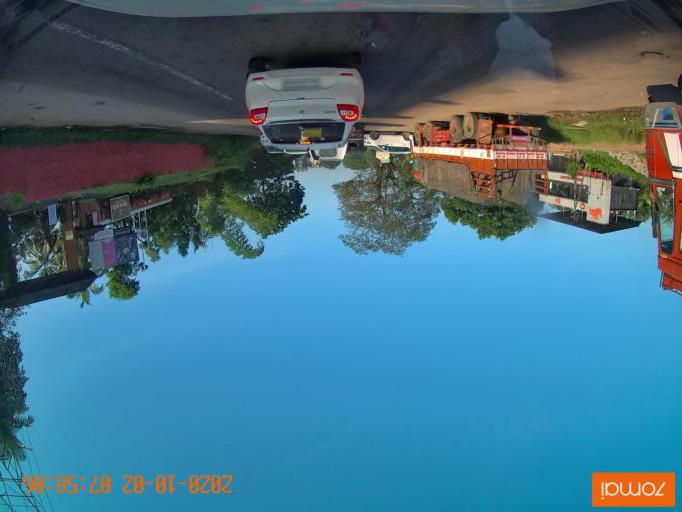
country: IN
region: Kerala
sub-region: Kozhikode
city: Ferokh
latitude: 11.2042
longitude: 75.8655
